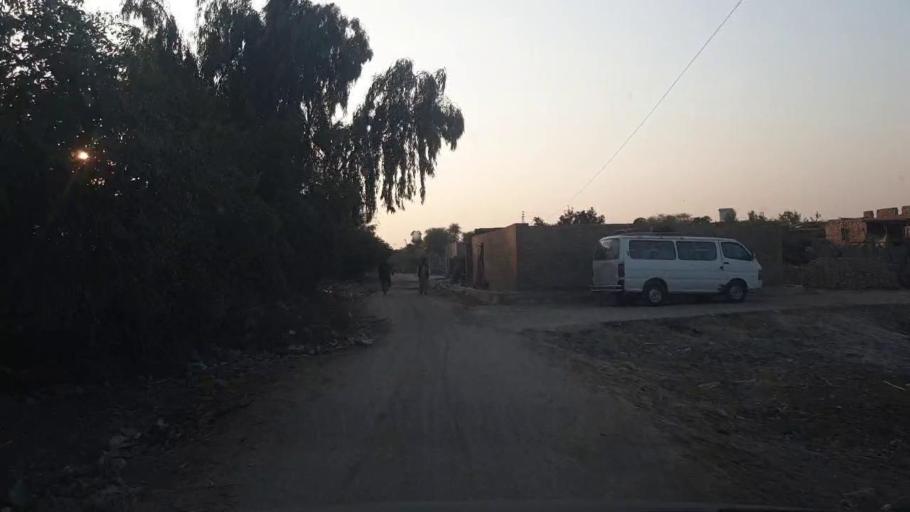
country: PK
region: Sindh
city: Bhit Shah
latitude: 25.8759
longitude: 68.5448
